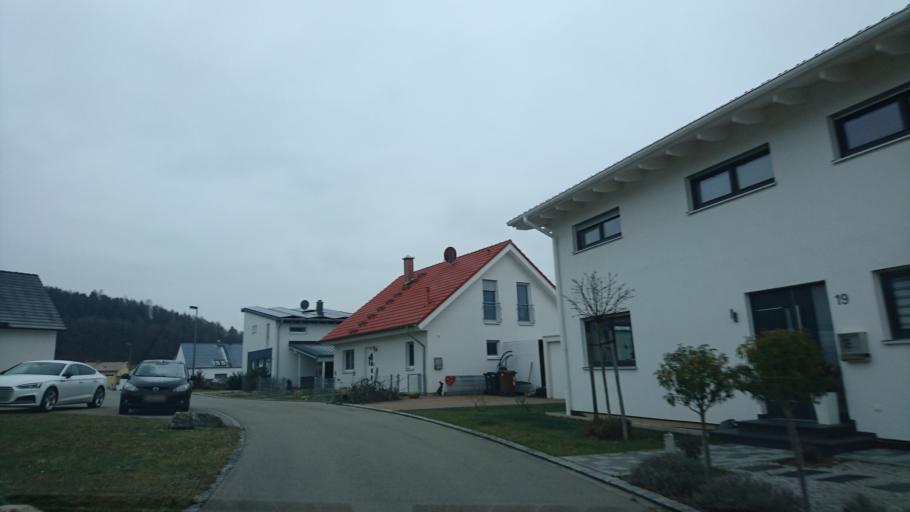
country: DE
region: Bavaria
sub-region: Swabia
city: Altenmunster
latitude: 48.4354
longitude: 10.6016
